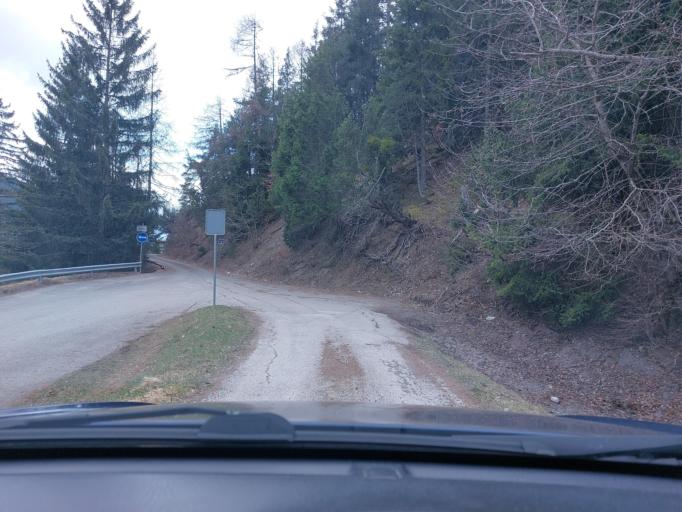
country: CH
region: Valais
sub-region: Sion District
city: Saviese
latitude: 46.2702
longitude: 7.3172
